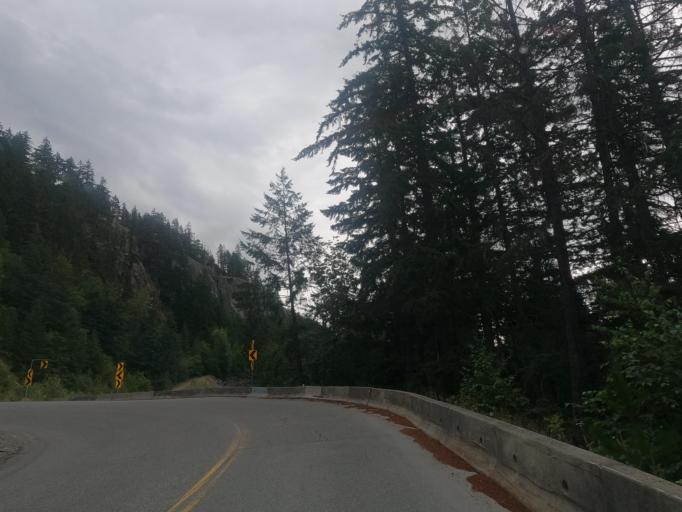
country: CA
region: British Columbia
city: Pemberton
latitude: 50.3000
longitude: -122.5834
